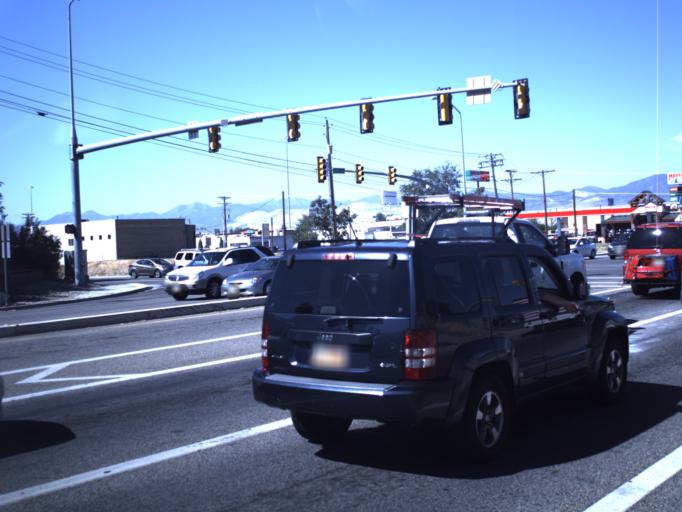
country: US
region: Utah
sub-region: Salt Lake County
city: Murray
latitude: 40.6746
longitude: -111.8983
